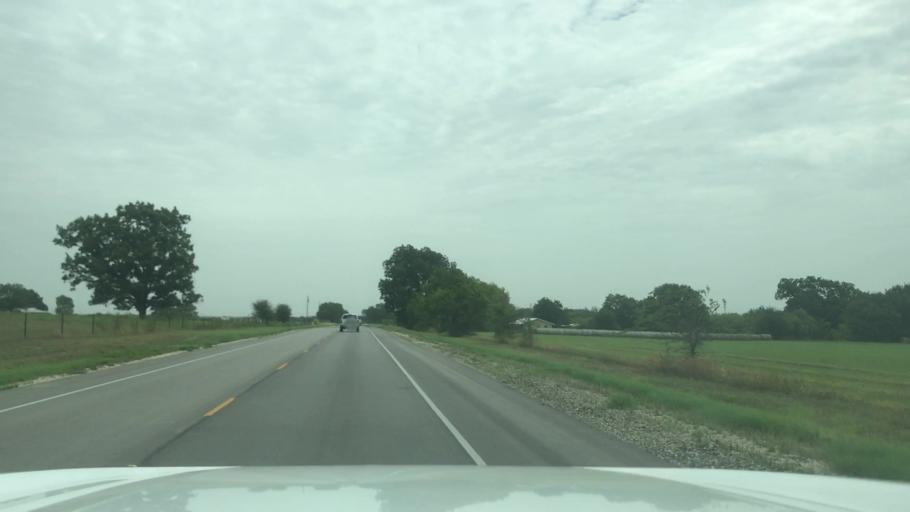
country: US
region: Texas
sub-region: Erath County
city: Dublin
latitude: 32.0903
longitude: -98.2829
